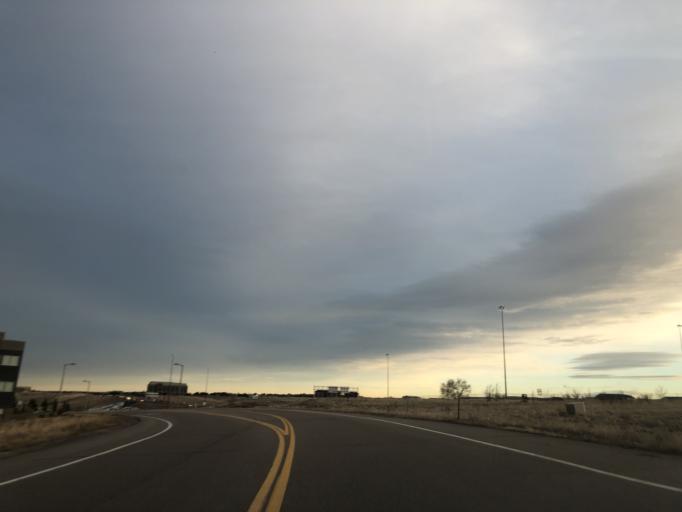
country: US
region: Colorado
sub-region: Douglas County
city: Meridian
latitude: 39.5577
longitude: -104.8684
